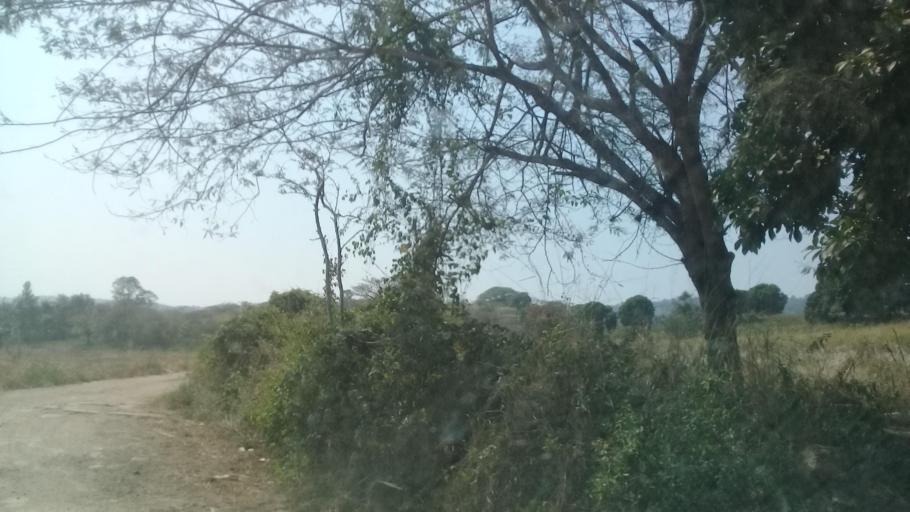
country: MX
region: Veracruz
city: El Castillo
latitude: 19.5686
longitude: -96.8355
